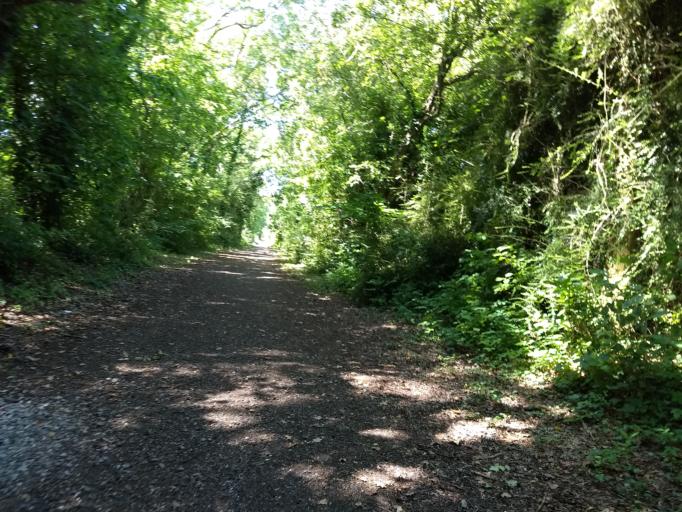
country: GB
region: England
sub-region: Isle of Wight
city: Newport
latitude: 50.7206
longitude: -1.2606
